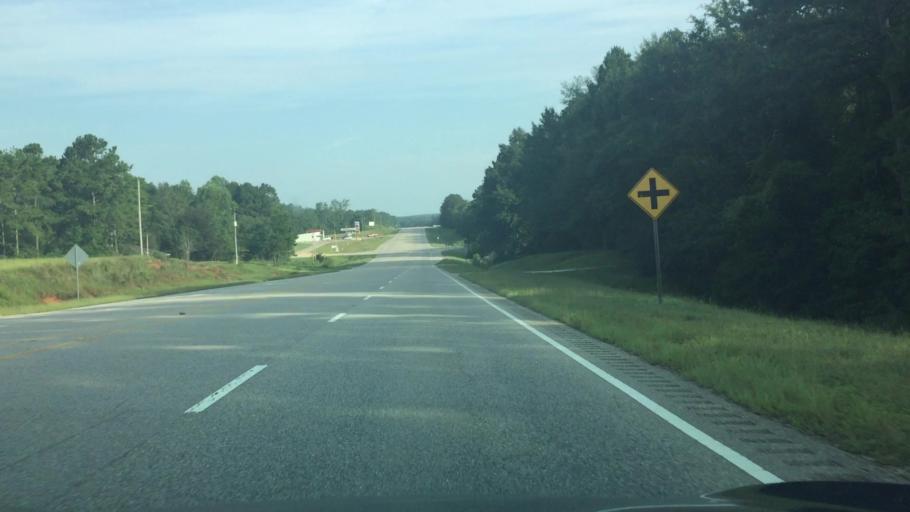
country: US
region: Alabama
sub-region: Butler County
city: Georgiana
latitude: 31.4851
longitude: -86.6800
